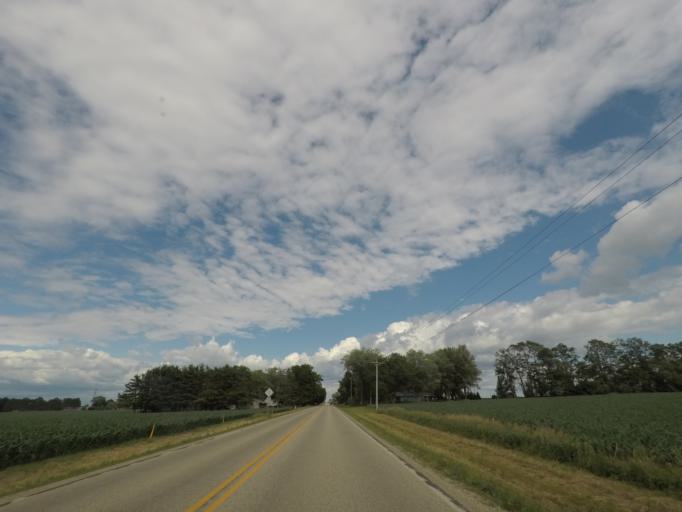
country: US
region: Wisconsin
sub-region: Rock County
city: Janesville
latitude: 42.7013
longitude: -89.1281
